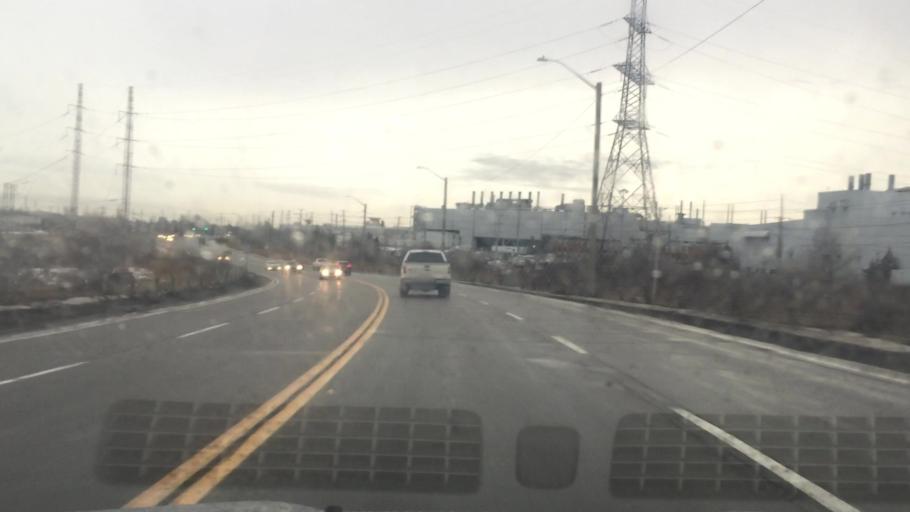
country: CA
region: Ontario
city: Oakville
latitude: 43.4861
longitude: -79.6586
